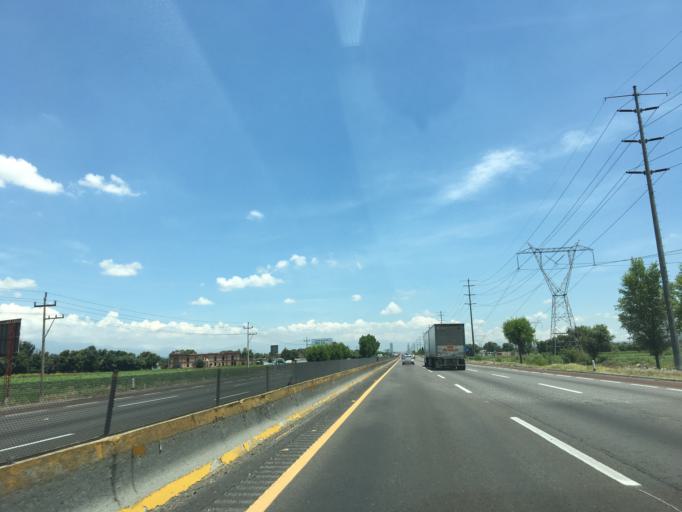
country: MX
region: Puebla
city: Tlaltenango
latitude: 19.1896
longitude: -98.3257
